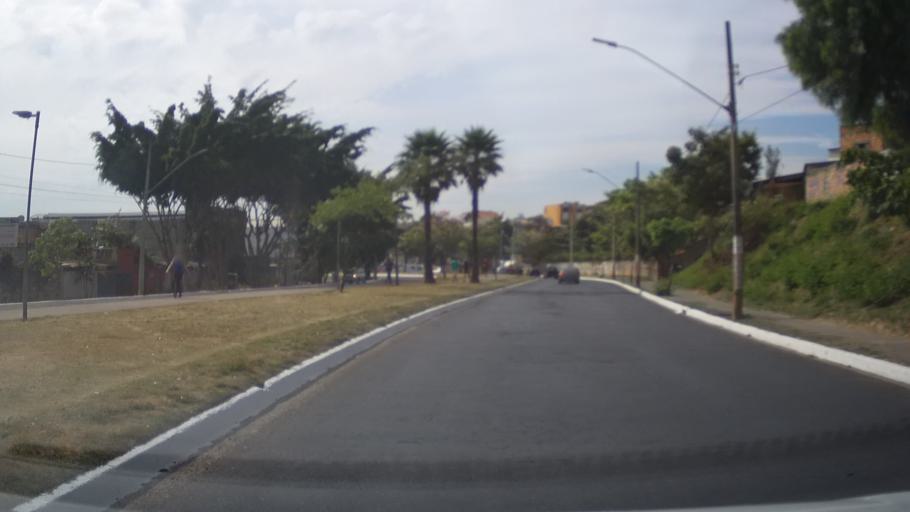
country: BR
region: Minas Gerais
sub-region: Contagem
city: Contagem
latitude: -19.9470
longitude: -44.0450
